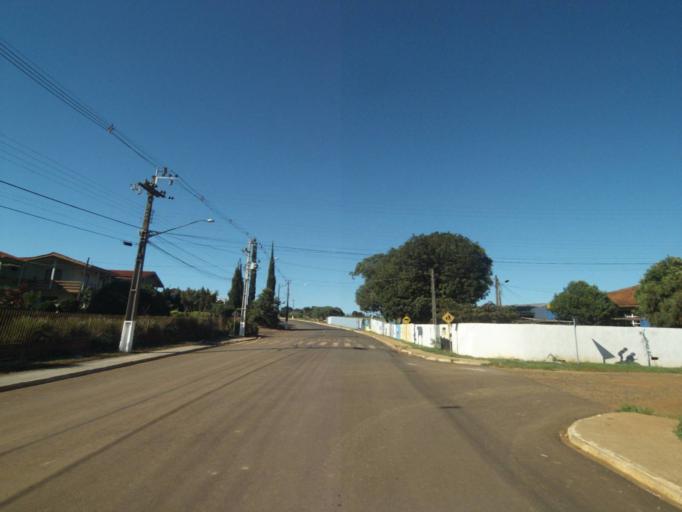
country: BR
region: Parana
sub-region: Pinhao
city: Pinhao
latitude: -25.8414
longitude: -52.0295
